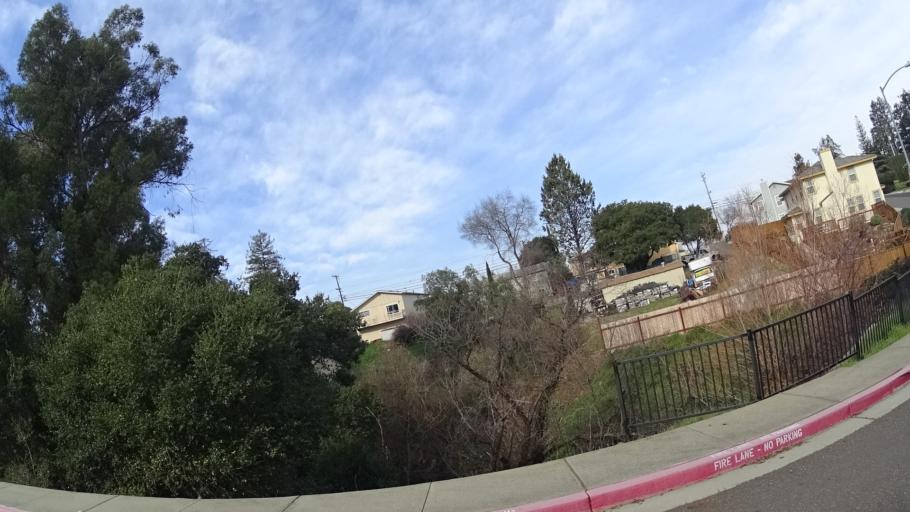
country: US
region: California
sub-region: Alameda County
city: Fairview
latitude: 37.6780
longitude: -122.0608
